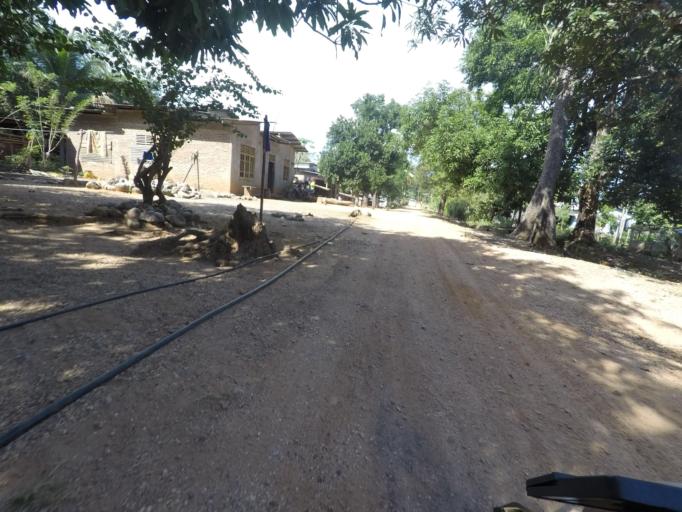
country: TL
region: Bobonaro
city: Maliana
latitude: -8.9603
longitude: 125.2184
